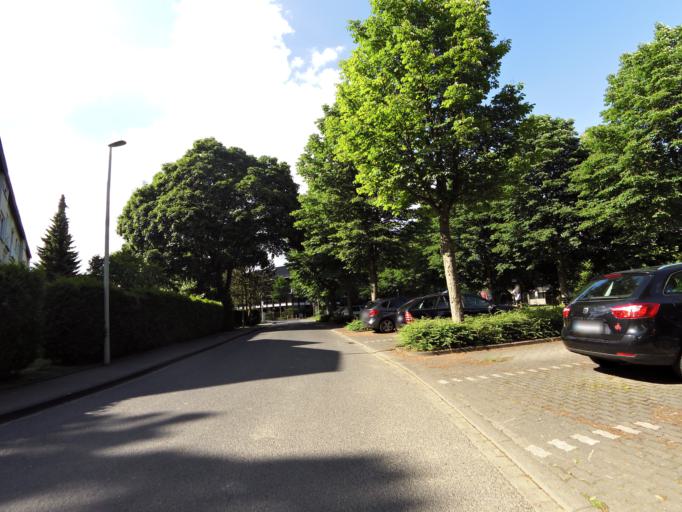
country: DE
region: North Rhine-Westphalia
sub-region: Regierungsbezirk Koln
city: Wachtberg
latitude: 50.6767
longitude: 7.0716
